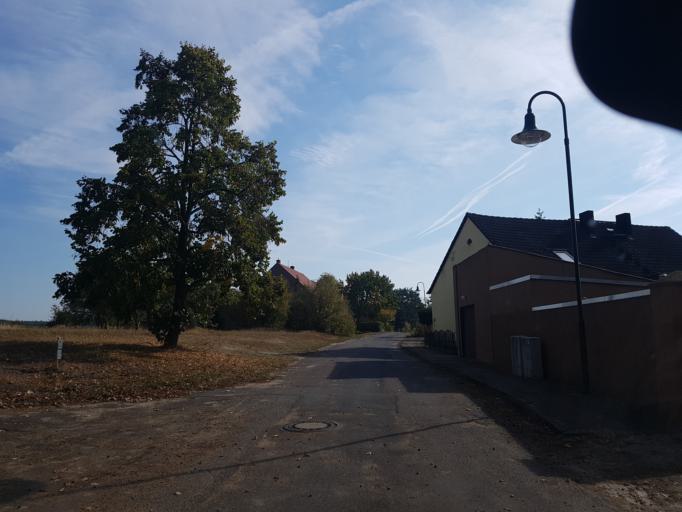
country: DE
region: Brandenburg
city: Ihlow
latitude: 51.8819
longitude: 13.2463
